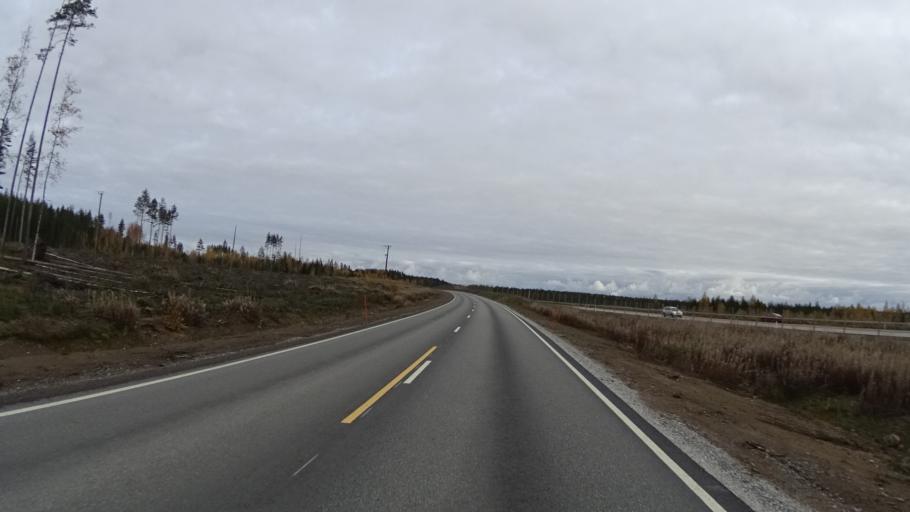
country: FI
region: South Karelia
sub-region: Lappeenranta
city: Lemi
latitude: 60.9970
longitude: 27.9331
